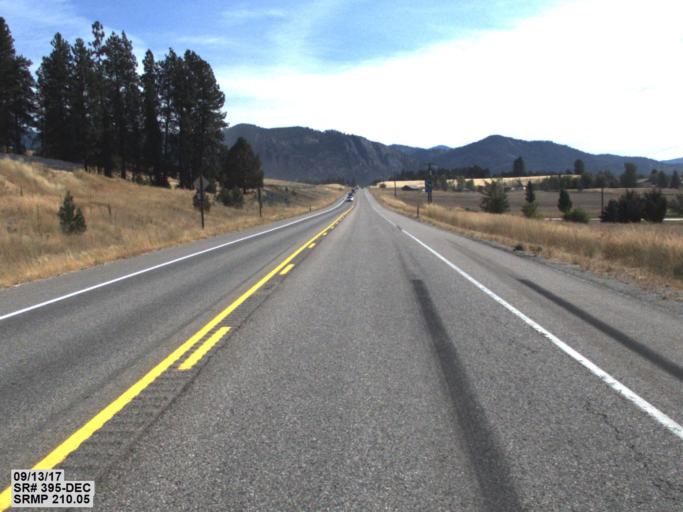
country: US
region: Washington
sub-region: Stevens County
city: Chewelah
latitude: 48.3002
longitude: -117.7615
